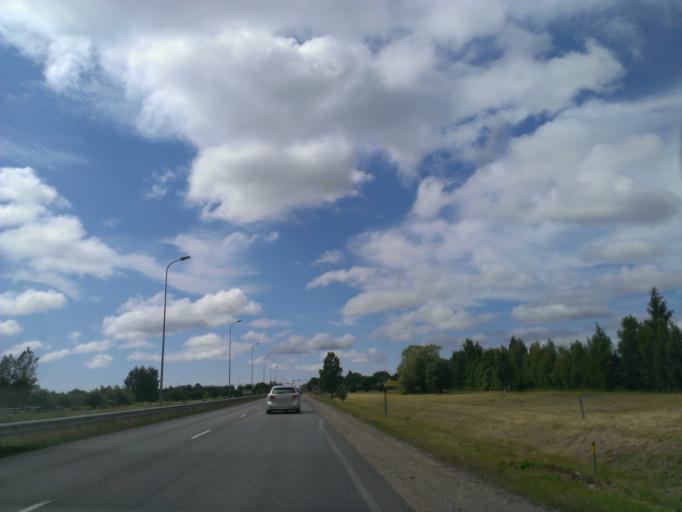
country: LV
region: Grobina
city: Grobina
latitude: 56.5384
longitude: 21.1782
